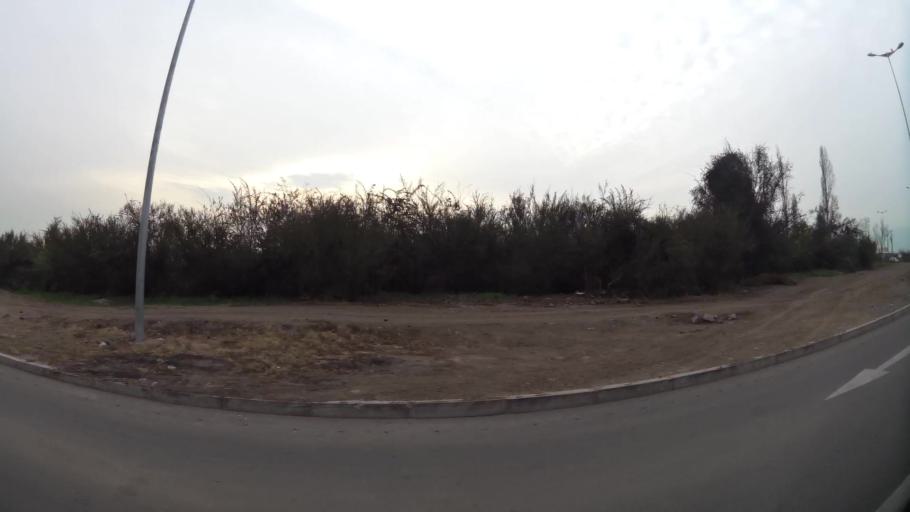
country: CL
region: Santiago Metropolitan
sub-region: Provincia de Chacabuco
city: Chicureo Abajo
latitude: -33.2622
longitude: -70.6187
